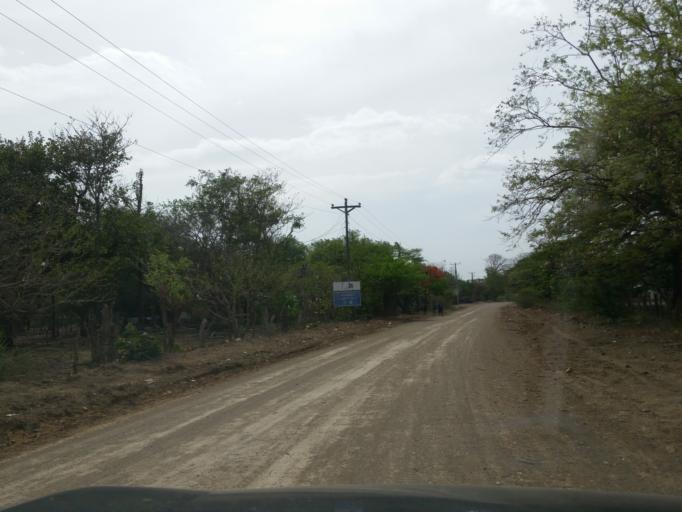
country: NI
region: Rivas
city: Tola
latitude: 11.4479
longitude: -86.0603
